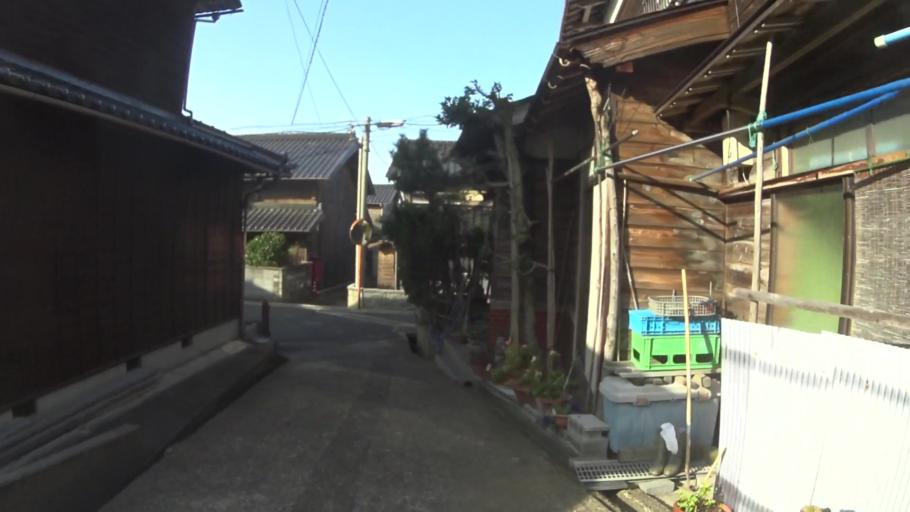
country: JP
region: Kyoto
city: Miyazu
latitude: 35.7632
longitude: 135.2060
